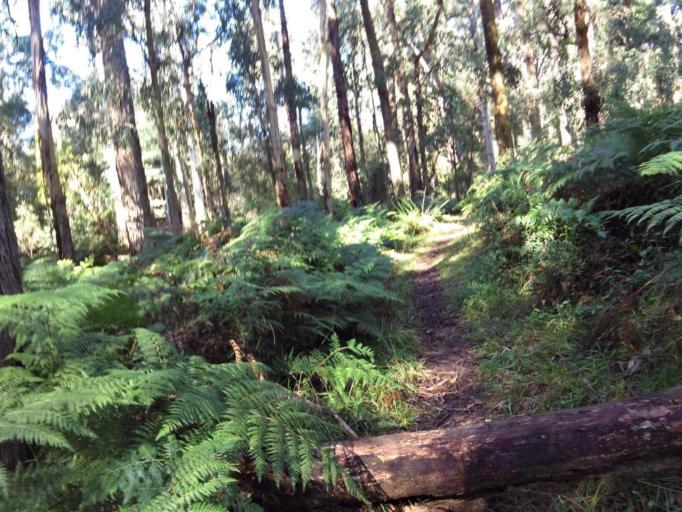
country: AU
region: Victoria
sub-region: Cardinia
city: Emerald
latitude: -37.8970
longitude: 145.4410
